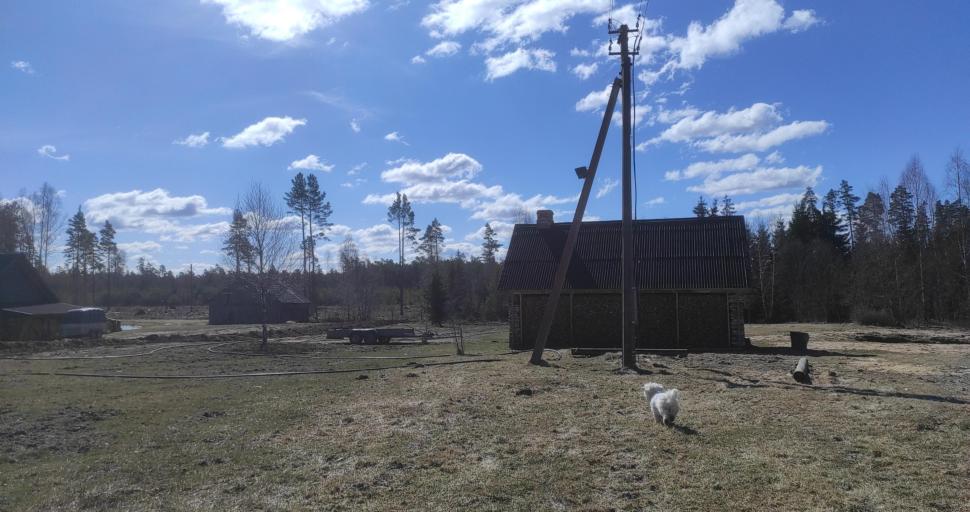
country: LV
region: Kuldigas Rajons
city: Kuldiga
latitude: 57.0537
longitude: 21.9567
